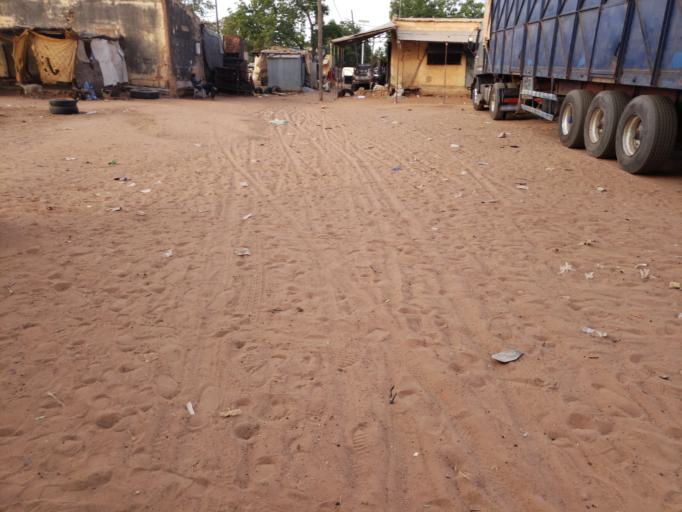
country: SN
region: Louga
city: Ndibene Dahra
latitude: 15.3919
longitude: -15.1135
